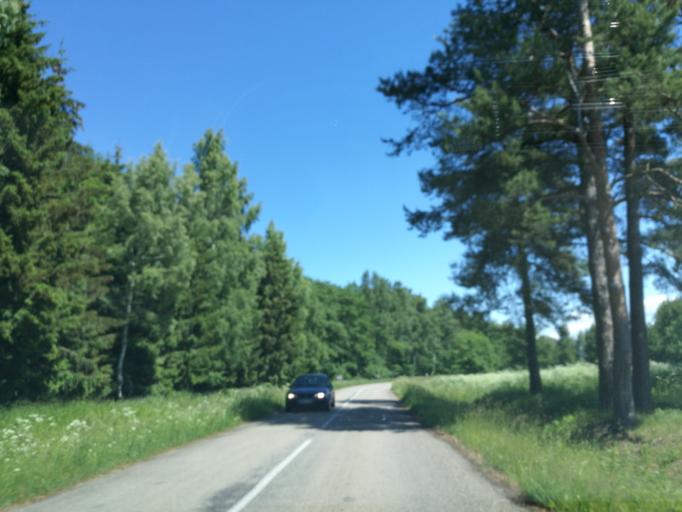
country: LT
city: Neringa
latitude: 55.3831
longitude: 21.2316
